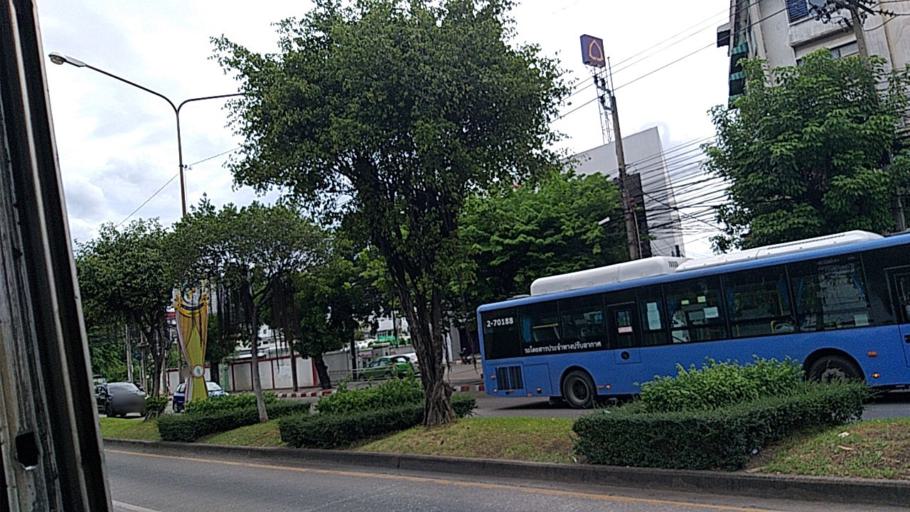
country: TH
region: Bangkok
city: Bueng Kum
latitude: 13.8052
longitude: 100.6479
